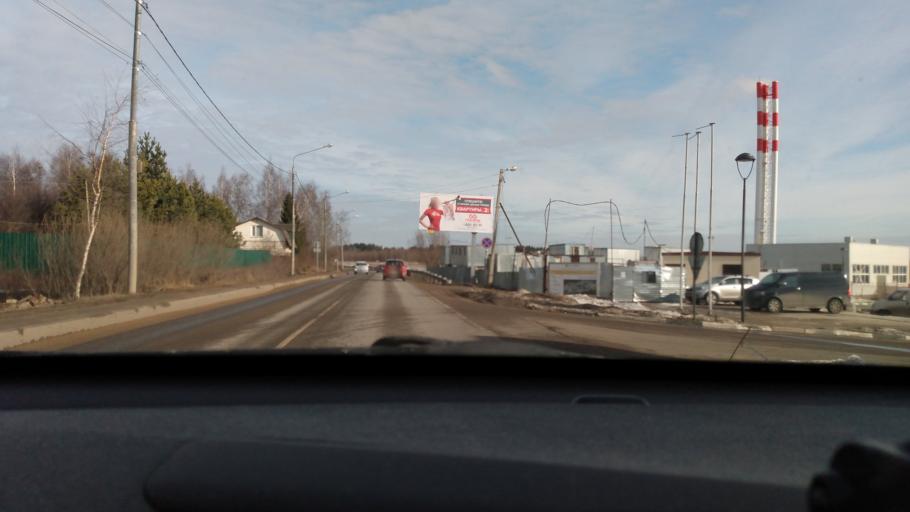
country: RU
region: Moskovskaya
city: Nakhabino
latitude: 55.8575
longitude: 37.1842
